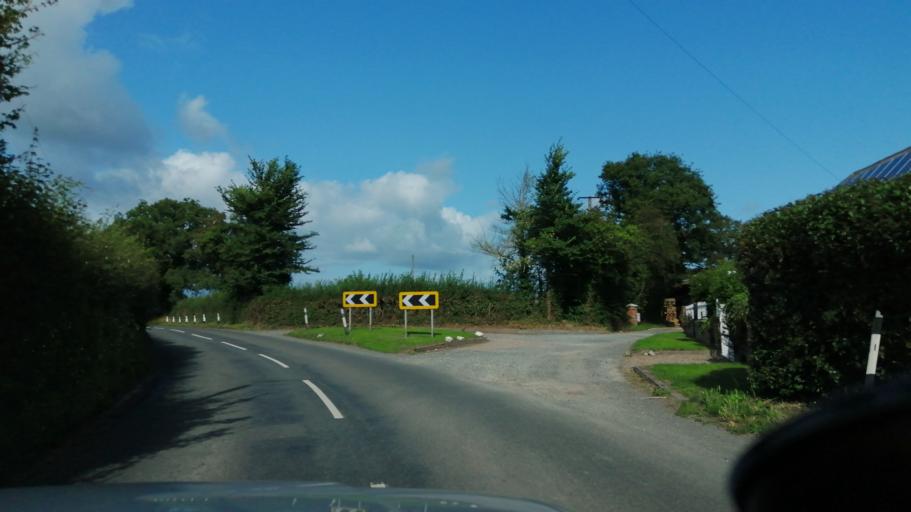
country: GB
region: England
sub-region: Herefordshire
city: Kingstone
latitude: 52.0382
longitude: -2.8173
